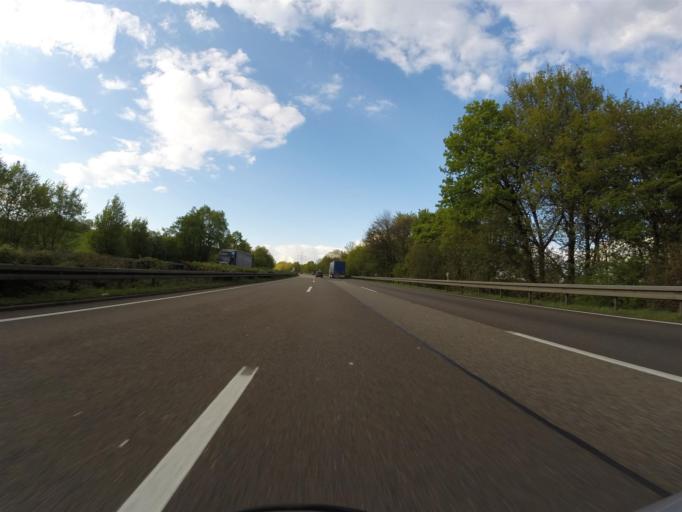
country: DE
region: Saarland
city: Sankt Ingbert
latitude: 49.2244
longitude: 7.0793
